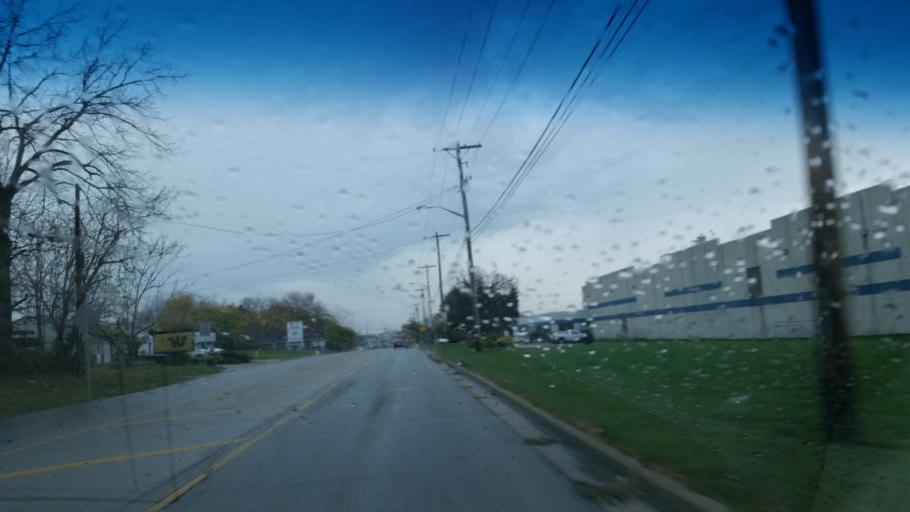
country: US
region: Indiana
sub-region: Howard County
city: Kokomo
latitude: 40.4763
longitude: -86.1529
